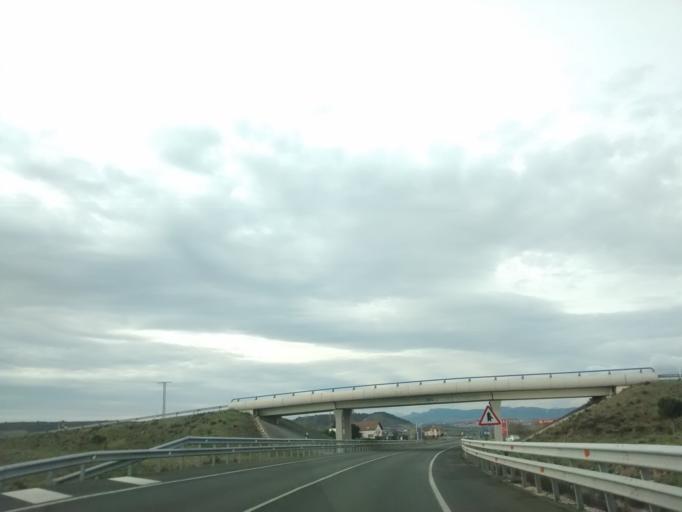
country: ES
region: La Rioja
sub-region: Provincia de La Rioja
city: San Asensio
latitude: 42.5123
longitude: -2.7385
